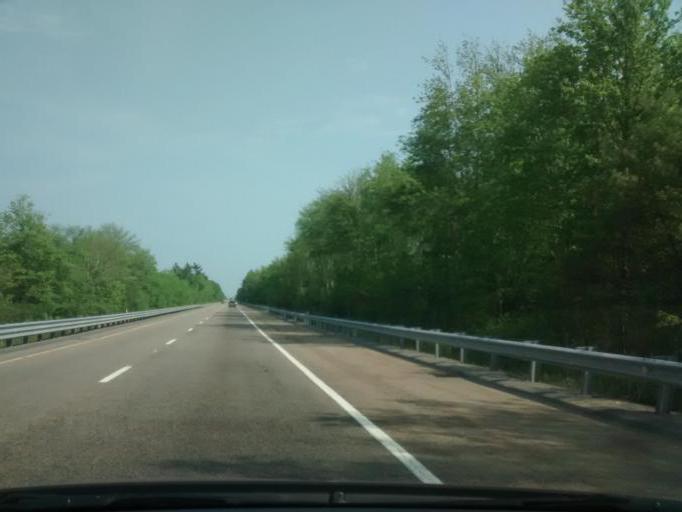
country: US
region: Massachusetts
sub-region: Plymouth County
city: West Wareham
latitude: 41.8314
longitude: -70.8173
